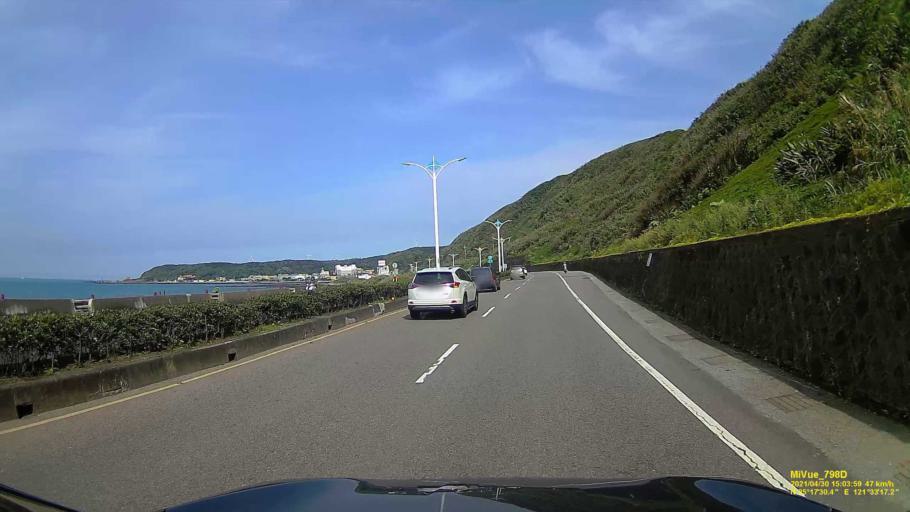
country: TW
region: Taipei
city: Taipei
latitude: 25.2917
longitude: 121.5551
